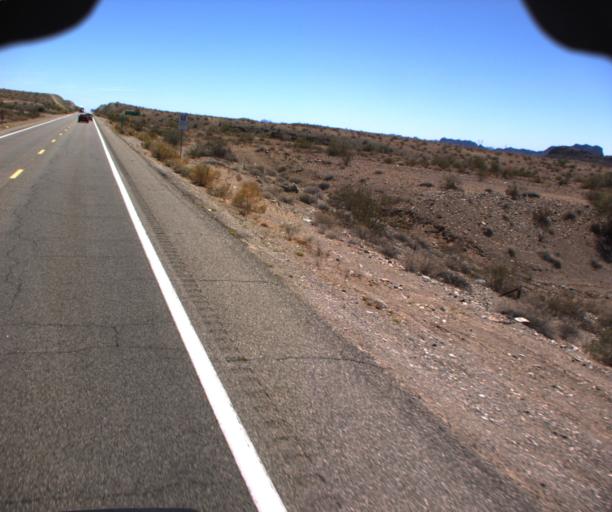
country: US
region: Arizona
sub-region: Mohave County
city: Lake Havasu City
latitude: 34.4348
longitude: -114.2206
